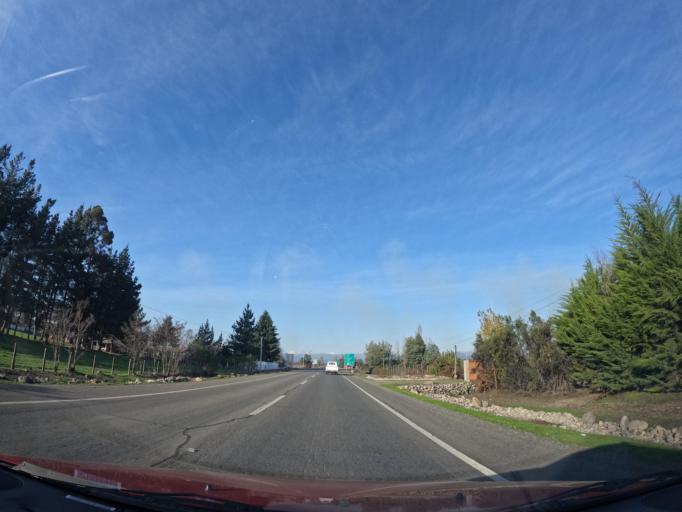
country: CL
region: Maule
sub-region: Provincia de Linares
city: Colbun
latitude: -35.6276
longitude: -71.4637
